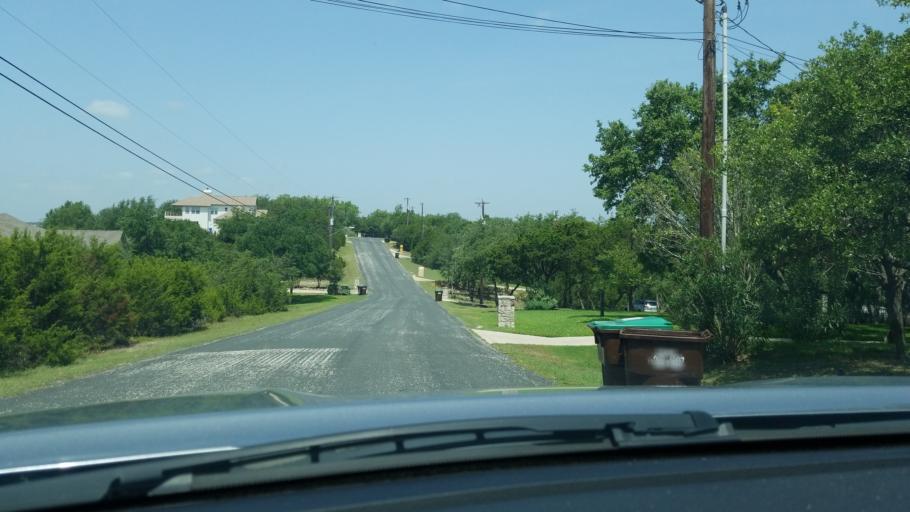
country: US
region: Texas
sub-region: Bexar County
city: Timberwood Park
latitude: 29.6930
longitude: -98.4840
